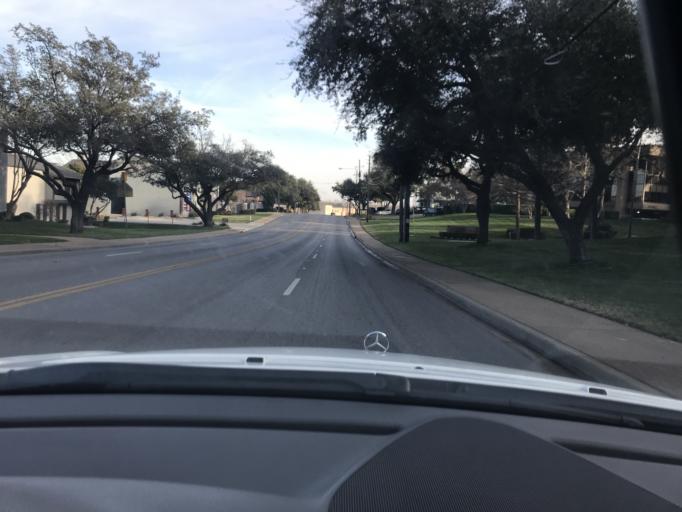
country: US
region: Texas
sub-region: Dallas County
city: University Park
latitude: 32.8867
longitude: -96.7614
